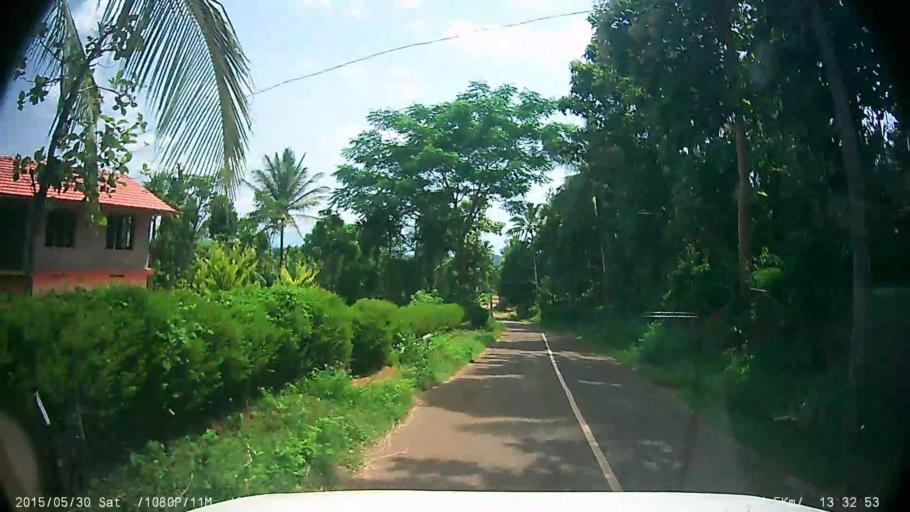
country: IN
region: Kerala
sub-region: Wayanad
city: Panamaram
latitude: 11.8198
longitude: 76.0762
